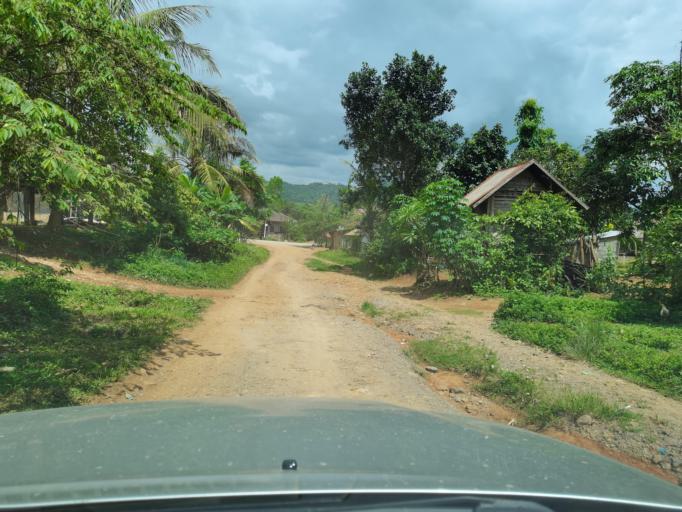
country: LA
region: Loungnamtha
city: Muang Long
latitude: 20.6800
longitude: 101.0567
